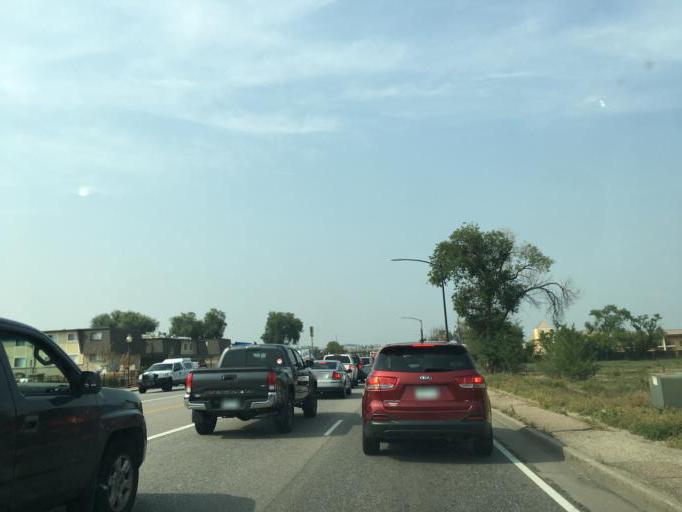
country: US
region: Colorado
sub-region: Jefferson County
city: Arvada
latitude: 39.7806
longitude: -105.1096
